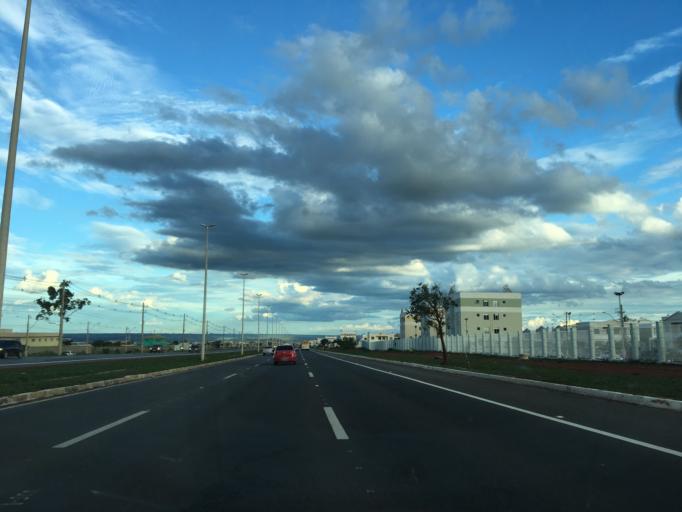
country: BR
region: Federal District
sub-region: Brasilia
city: Brasilia
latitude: -15.8857
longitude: -47.8153
